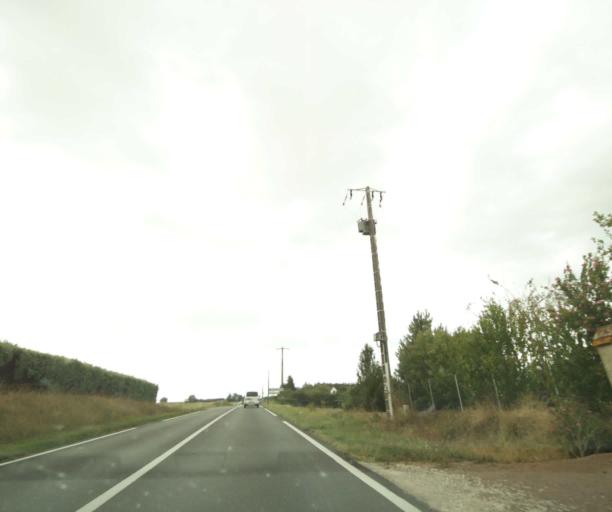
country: FR
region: Centre
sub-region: Departement d'Indre-et-Loire
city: Chambourg-sur-Indre
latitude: 47.1801
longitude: 0.9634
